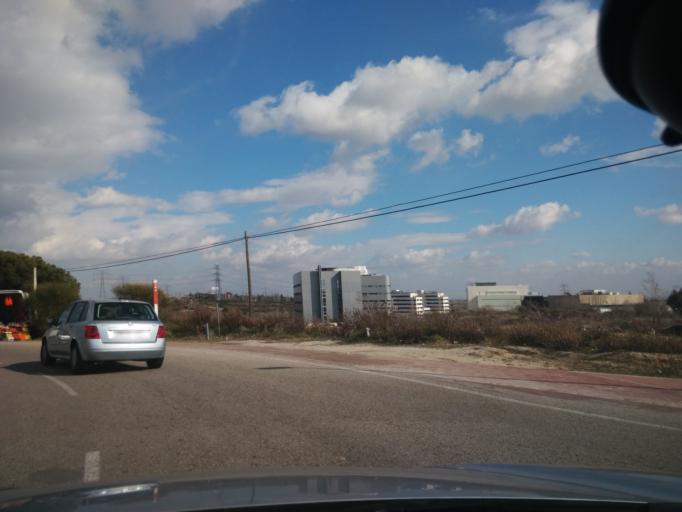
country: ES
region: Madrid
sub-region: Provincia de Madrid
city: Las Tablas
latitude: 40.5498
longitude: -3.6943
